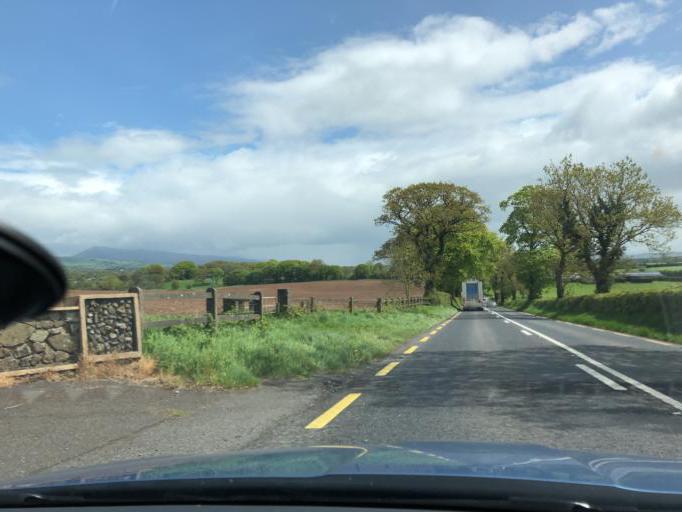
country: IE
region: Munster
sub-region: County Cork
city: Mitchelstown
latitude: 52.2504
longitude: -8.3913
